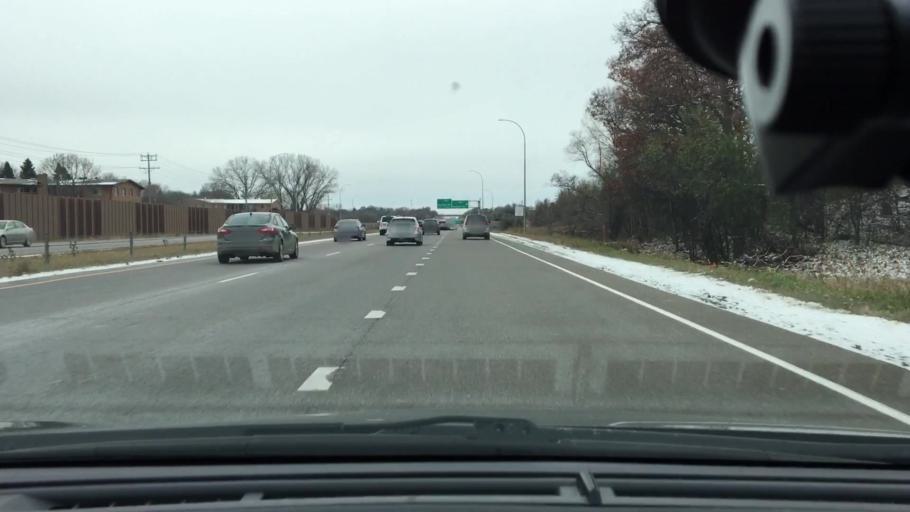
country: US
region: Minnesota
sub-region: Hennepin County
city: New Hope
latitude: 45.0395
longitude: -93.4010
